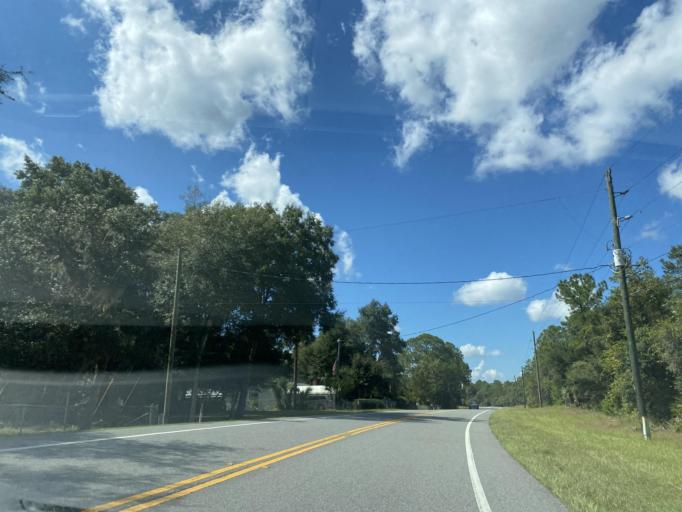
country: US
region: Florida
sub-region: Lake County
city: Lake Mack-Forest Hills
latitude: 29.0045
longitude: -81.4357
